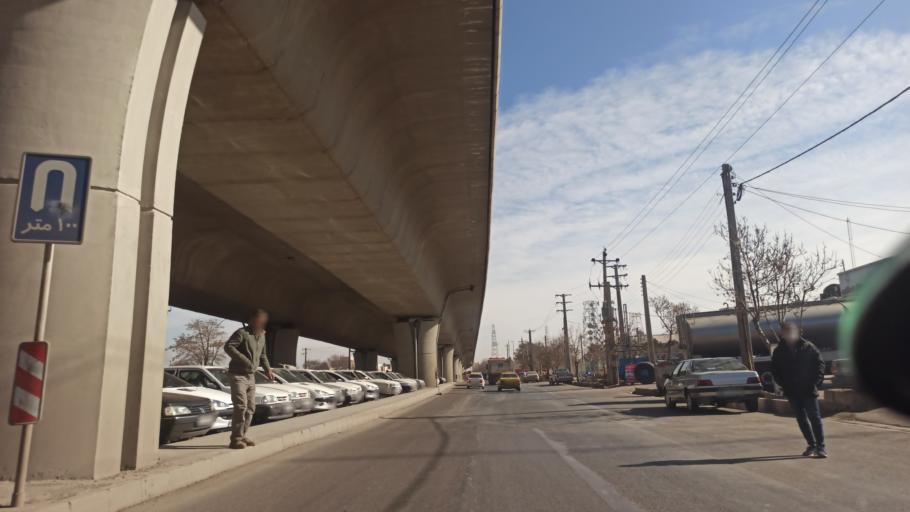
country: IR
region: Qazvin
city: Qazvin
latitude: 36.2555
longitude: 49.9986
